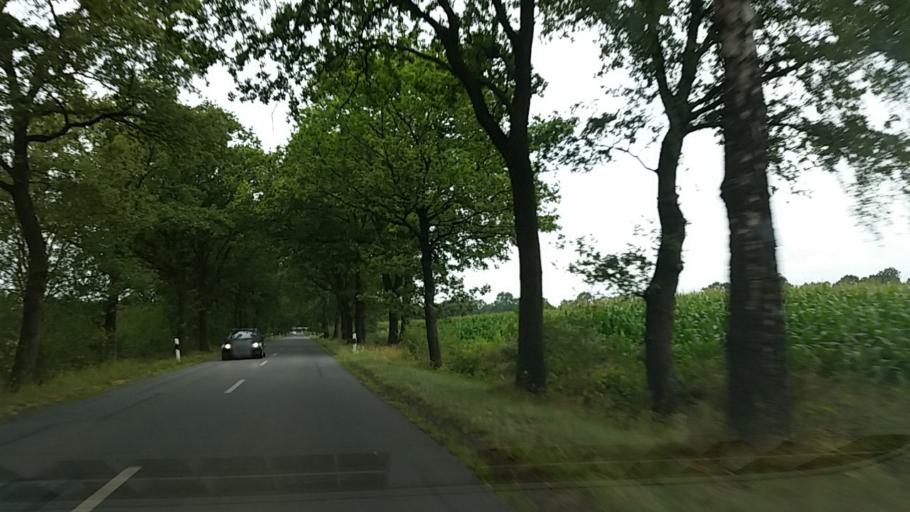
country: DE
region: Lower Saxony
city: Hipstedt
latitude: 53.4220
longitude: 8.9068
